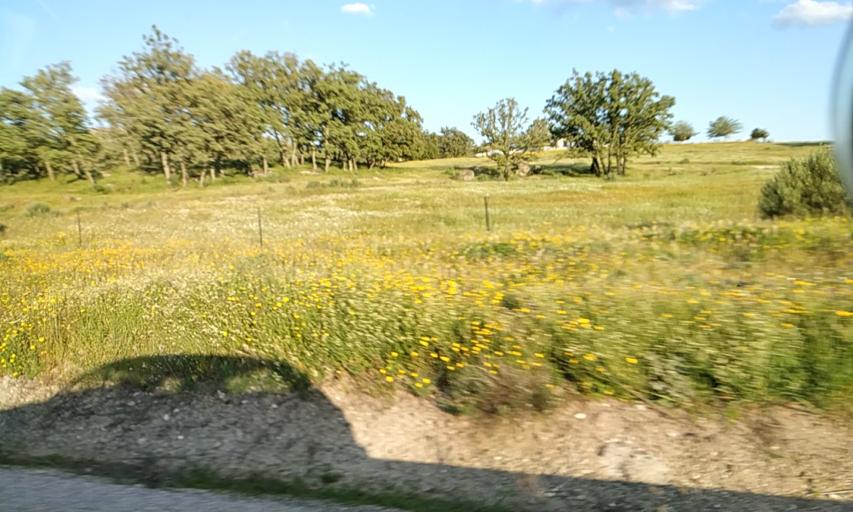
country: ES
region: Extremadura
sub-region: Provincia de Caceres
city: Valencia de Alcantara
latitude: 39.3736
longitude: -7.2592
